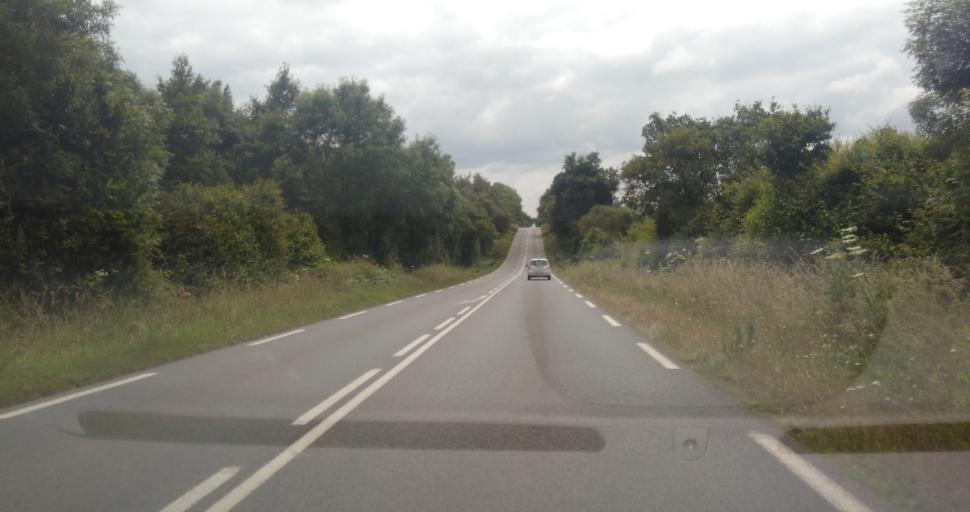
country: FR
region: Pays de la Loire
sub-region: Departement de la Vendee
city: Bournezeau
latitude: 46.6143
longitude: -1.1481
